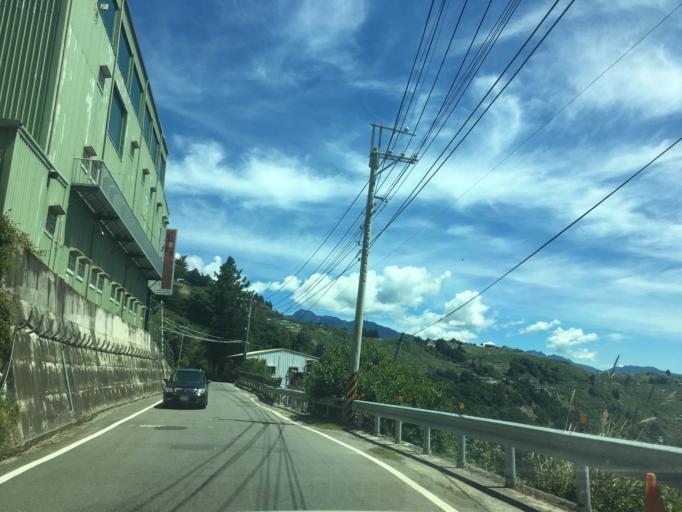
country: TW
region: Taiwan
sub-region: Nantou
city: Puli
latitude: 24.2414
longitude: 121.2556
